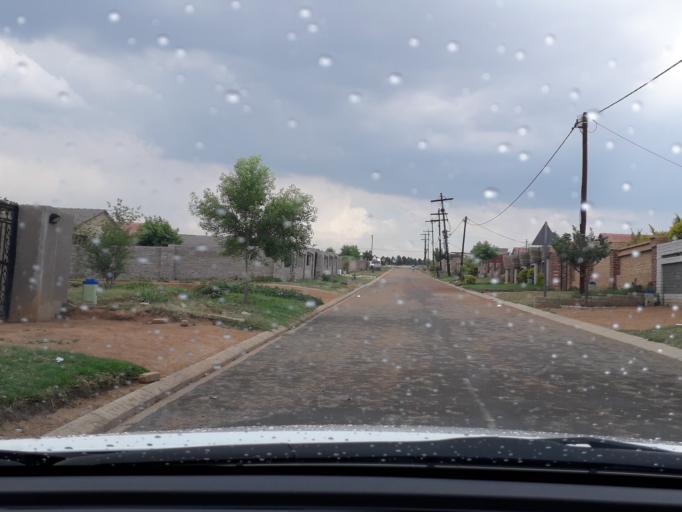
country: ZA
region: Gauteng
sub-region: West Rand District Municipality
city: Muldersdriseloop
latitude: -26.0062
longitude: 27.8522
